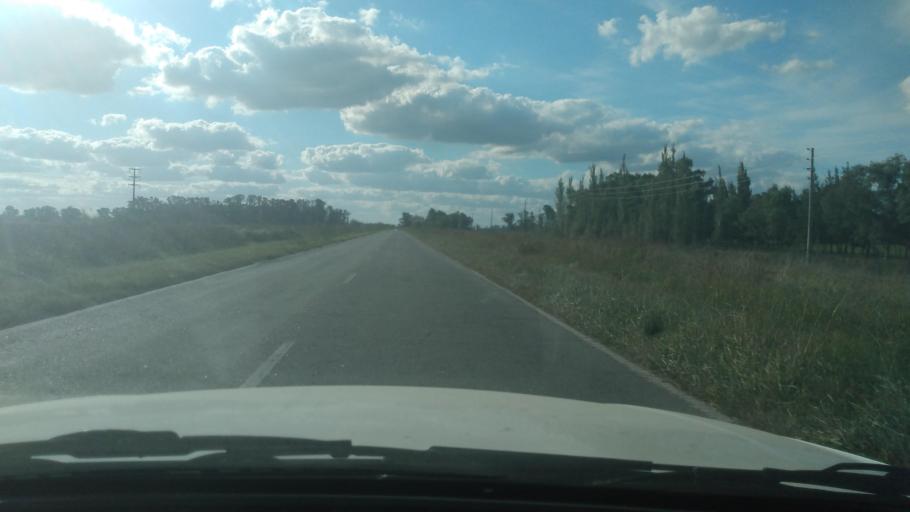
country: AR
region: Buenos Aires
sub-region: Partido de Mercedes
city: Mercedes
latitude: -34.7489
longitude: -59.3814
